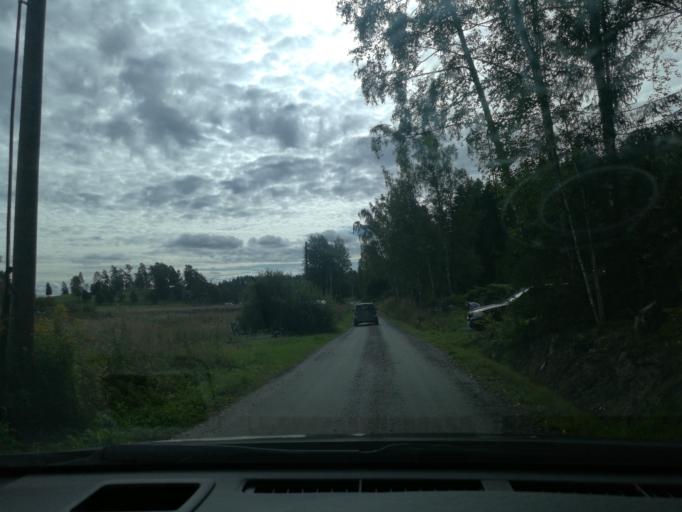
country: SE
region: OEstergoetland
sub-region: Soderkopings Kommun
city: Soederkoeping
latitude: 58.4863
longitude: 16.4720
